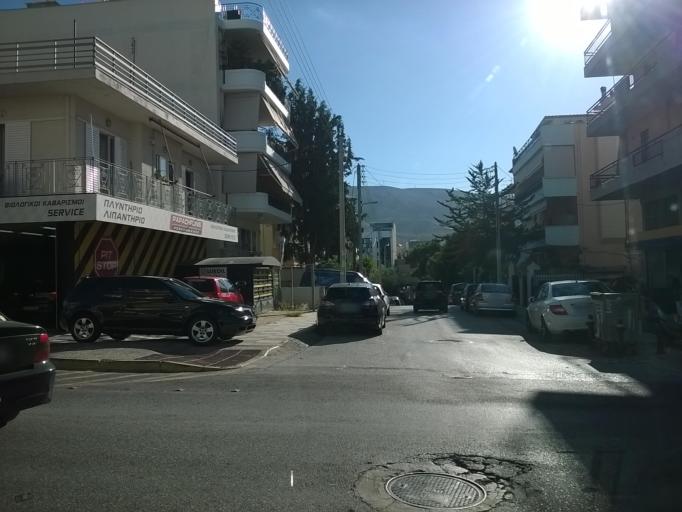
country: GR
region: Attica
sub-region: Nomarchia Athinas
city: Dhafni
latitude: 37.9430
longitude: 23.7381
